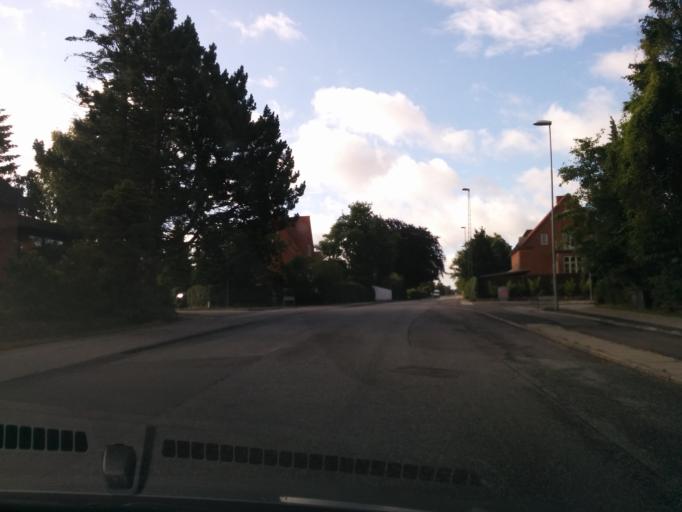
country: DK
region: Central Jutland
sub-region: Arhus Kommune
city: Arhus
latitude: 56.1355
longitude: 10.1786
